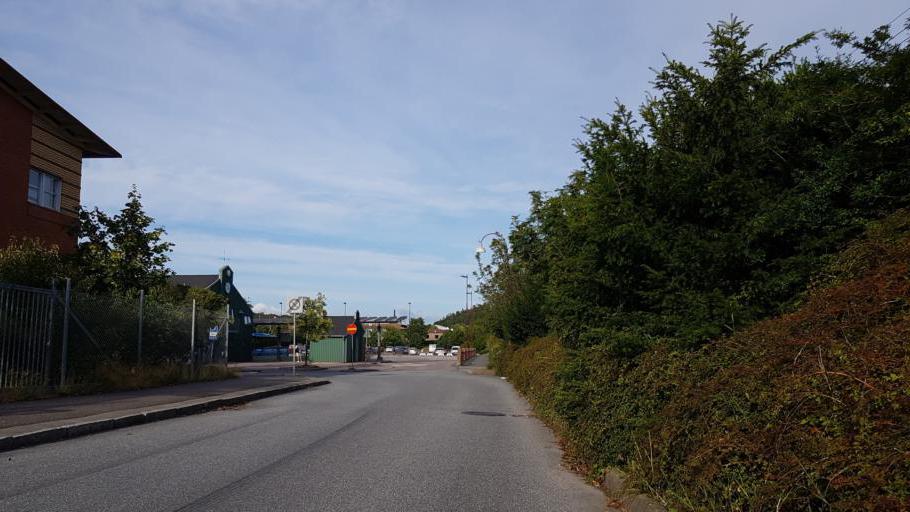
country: SE
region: Vaestra Goetaland
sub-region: Harryda Kommun
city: Molnlycke
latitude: 57.6566
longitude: 12.1164
